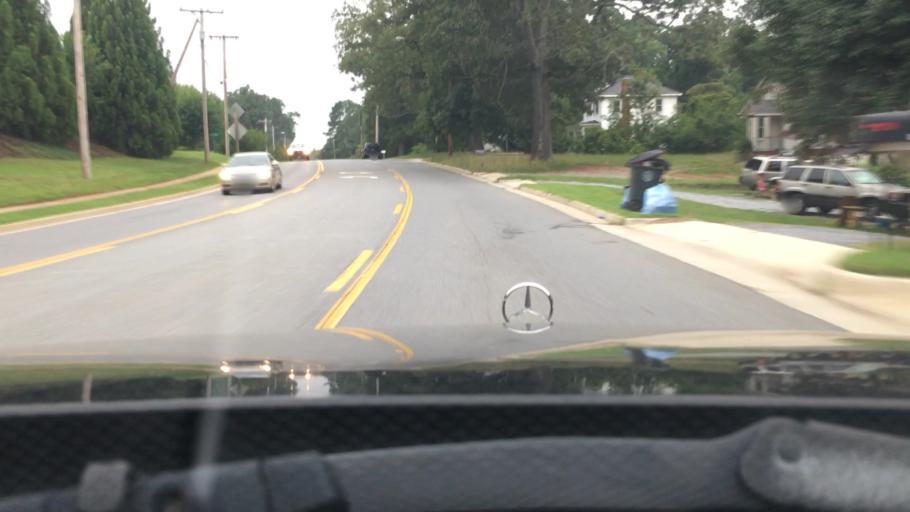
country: US
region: Virginia
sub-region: Campbell County
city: Timberlake
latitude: 37.3568
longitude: -79.2266
